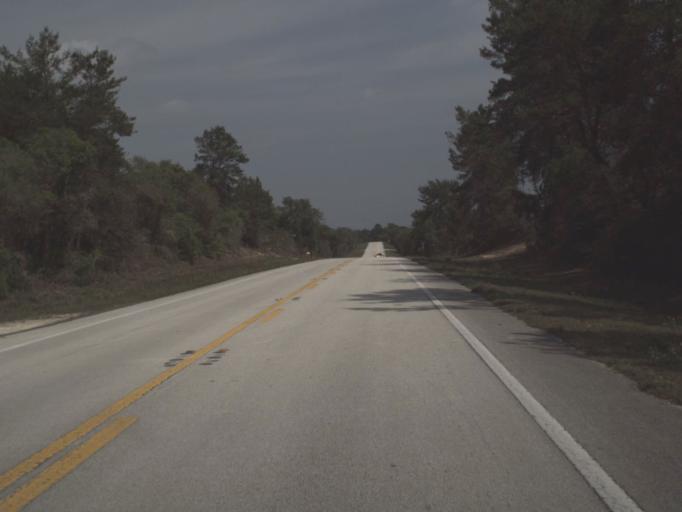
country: US
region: Florida
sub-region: Lake County
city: Astor
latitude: 29.2685
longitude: -81.6466
